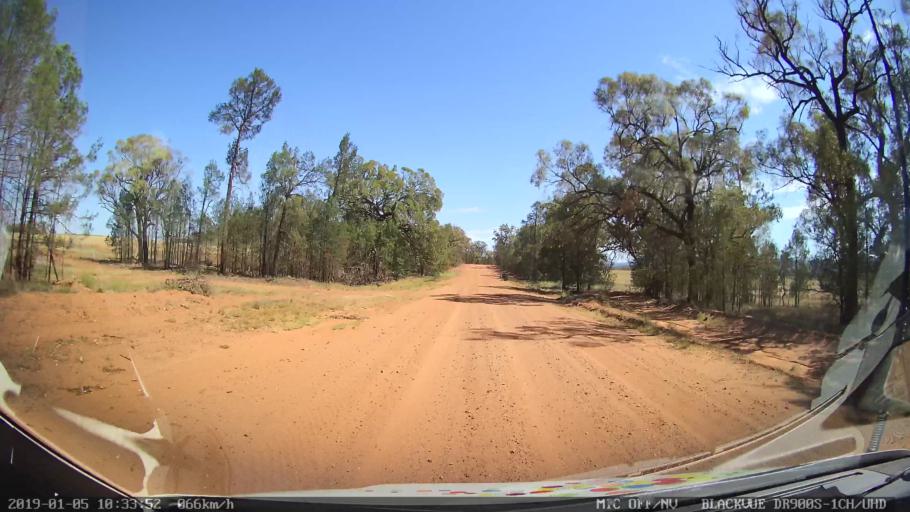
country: AU
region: New South Wales
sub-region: Gilgandra
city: Gilgandra
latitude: -31.5034
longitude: 148.9295
